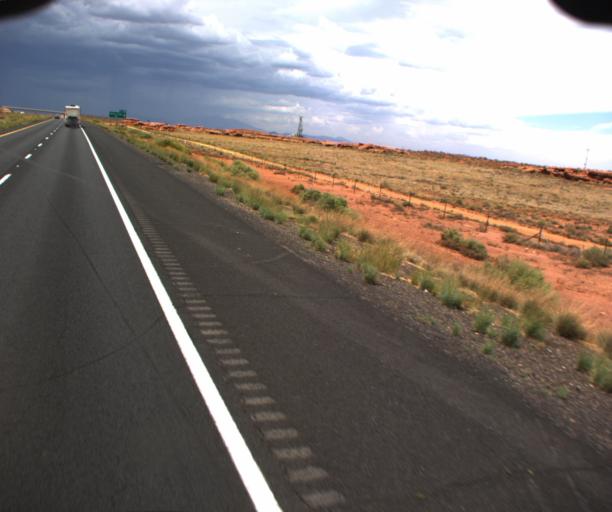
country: US
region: Arizona
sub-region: Coconino County
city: LeChee
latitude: 35.1092
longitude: -111.0215
